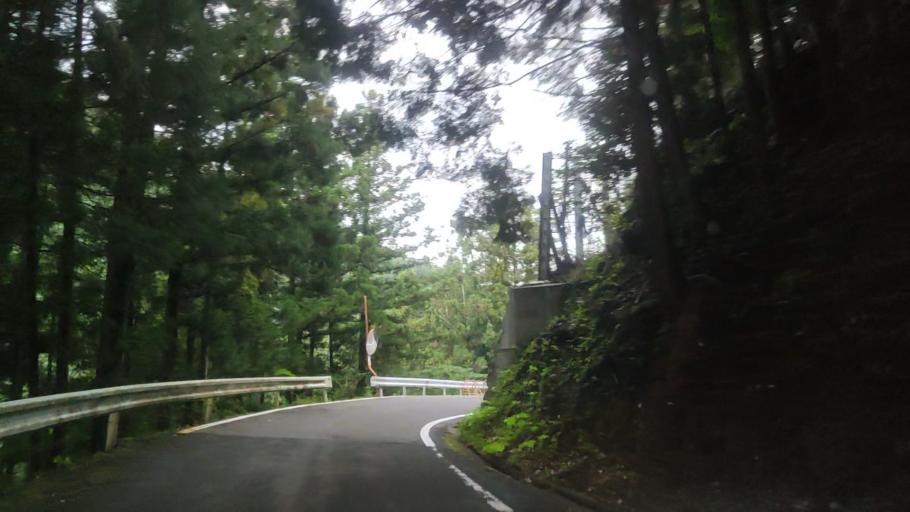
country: JP
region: Wakayama
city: Hashimoto
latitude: 34.2740
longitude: 135.6353
